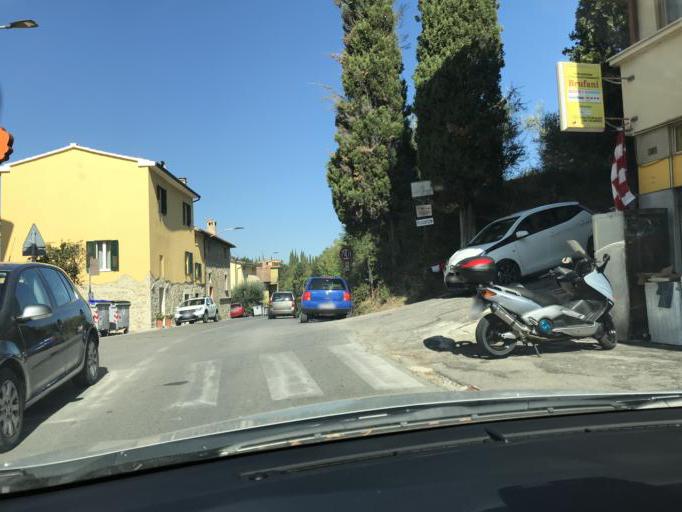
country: IT
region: Umbria
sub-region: Provincia di Perugia
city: Ponte Felcino
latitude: 43.1065
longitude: 12.4318
